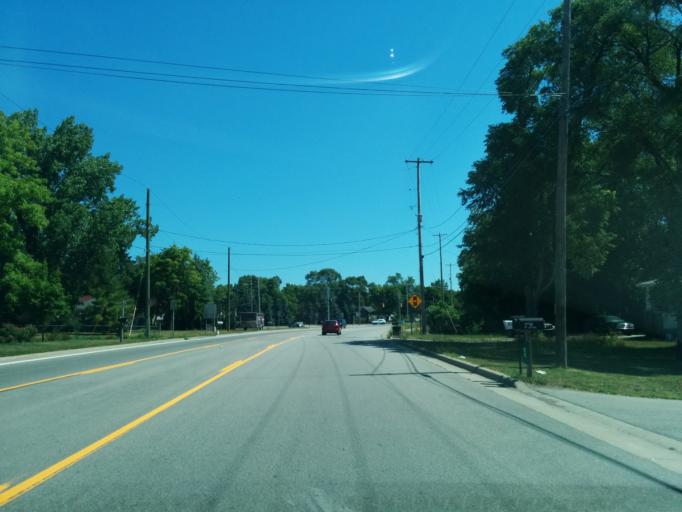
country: US
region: Michigan
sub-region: Bay County
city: Bay City
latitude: 43.5790
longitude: -83.9220
